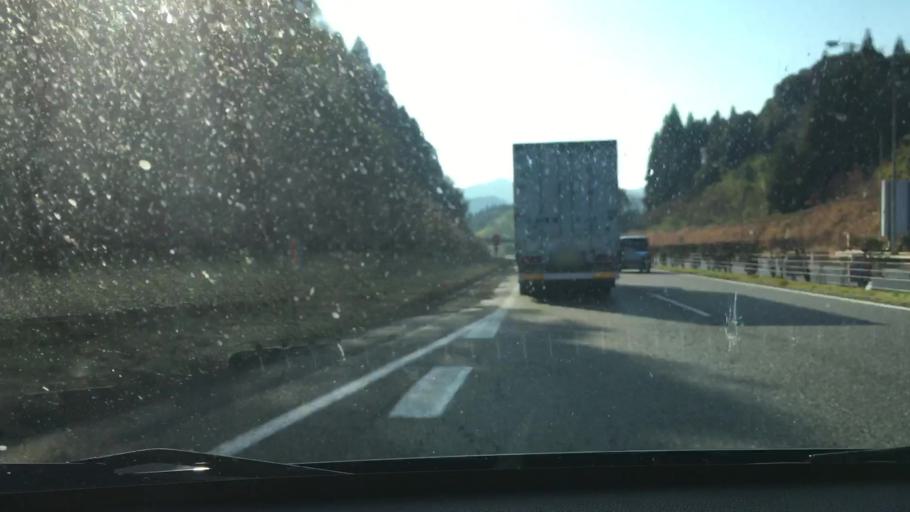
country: JP
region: Kagoshima
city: Okuchi-shinohara
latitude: 31.9439
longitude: 130.7192
